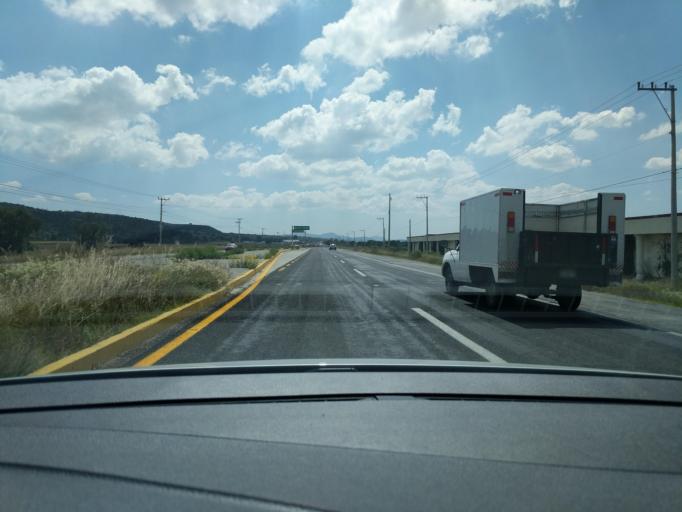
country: MX
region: Hidalgo
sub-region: Mineral de la Reforma
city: Rinconada de los Angeles
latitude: 20.0075
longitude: -98.7150
